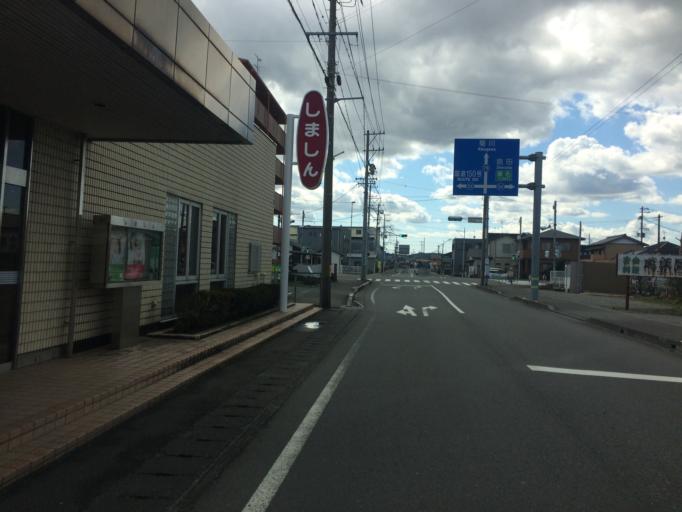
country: JP
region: Shizuoka
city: Shimada
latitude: 34.7878
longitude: 138.2446
